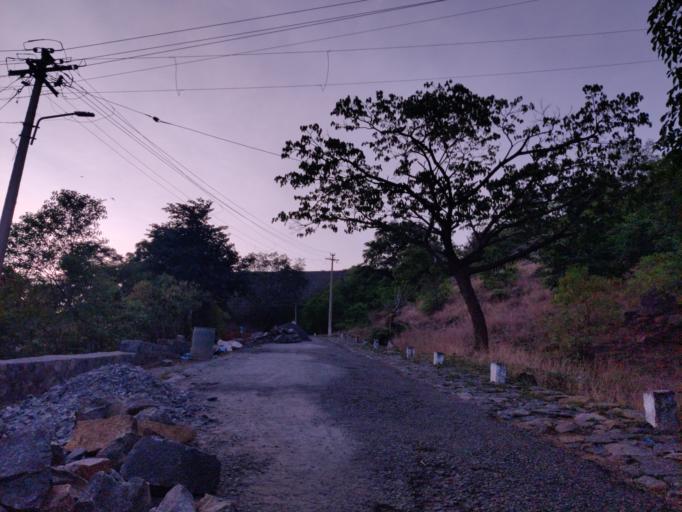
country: IN
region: Tamil Nadu
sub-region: Salem
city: Salem
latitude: 11.6212
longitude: 78.1504
